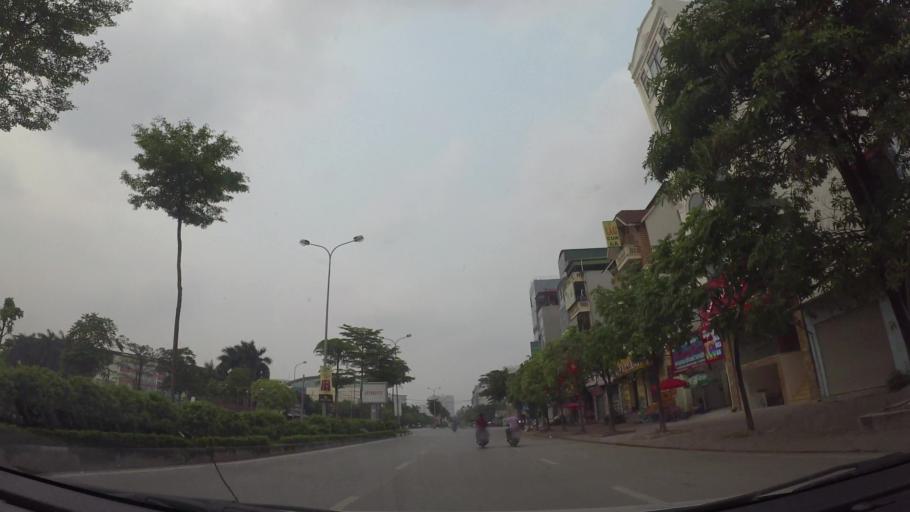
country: VN
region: Ha Noi
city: Cau Dien
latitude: 21.0419
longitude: 105.7735
